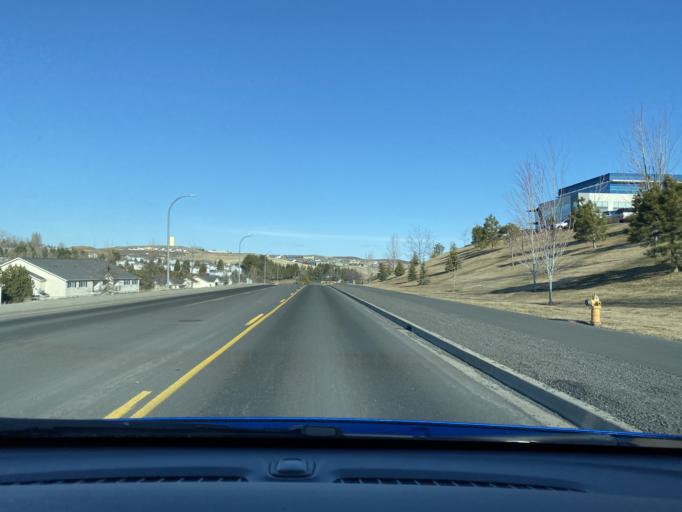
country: US
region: Washington
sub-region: Whitman County
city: Pullman
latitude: 46.7467
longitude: -117.1686
